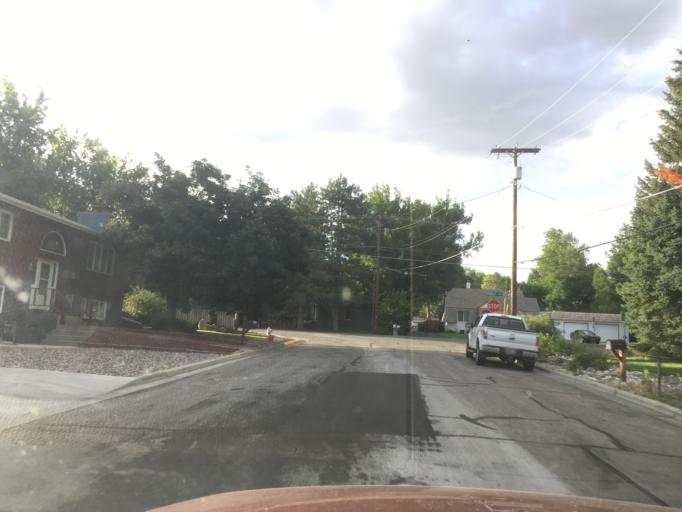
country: US
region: Montana
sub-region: Yellowstone County
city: Billings
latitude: 45.7945
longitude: -108.5696
